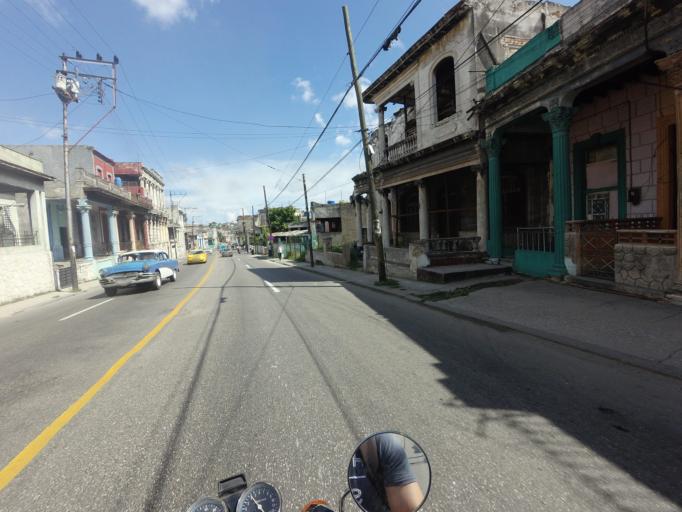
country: CU
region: La Habana
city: Diez de Octubre
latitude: 23.0918
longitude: -82.3644
